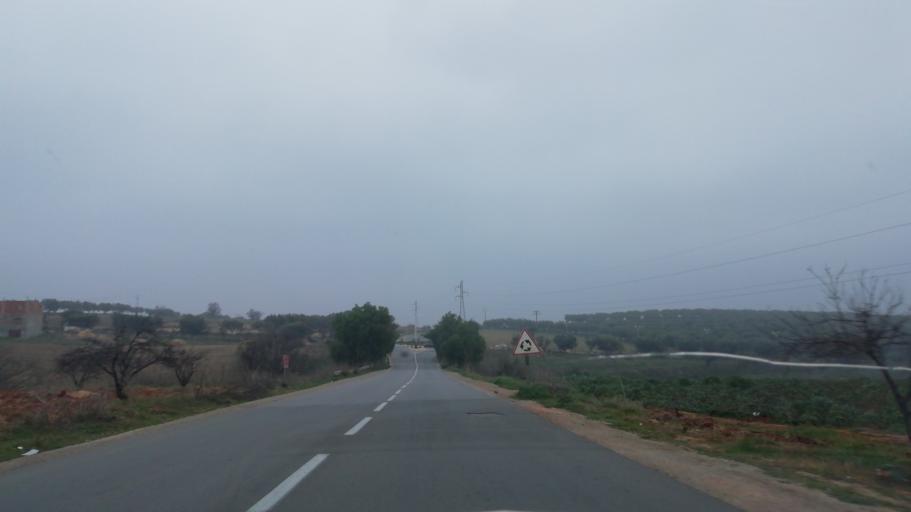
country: DZ
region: Mascara
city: Mascara
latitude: 35.4007
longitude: 0.1642
